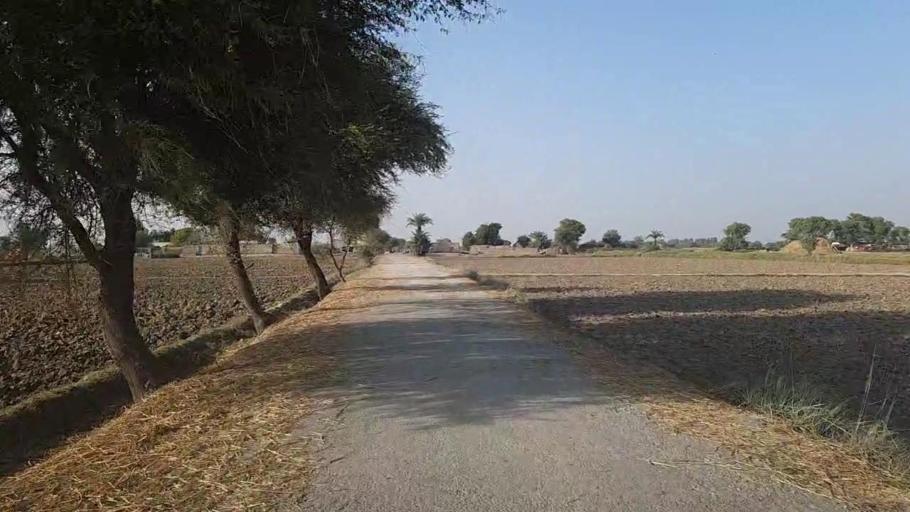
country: PK
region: Sindh
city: Kashmor
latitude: 28.4117
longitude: 69.4118
